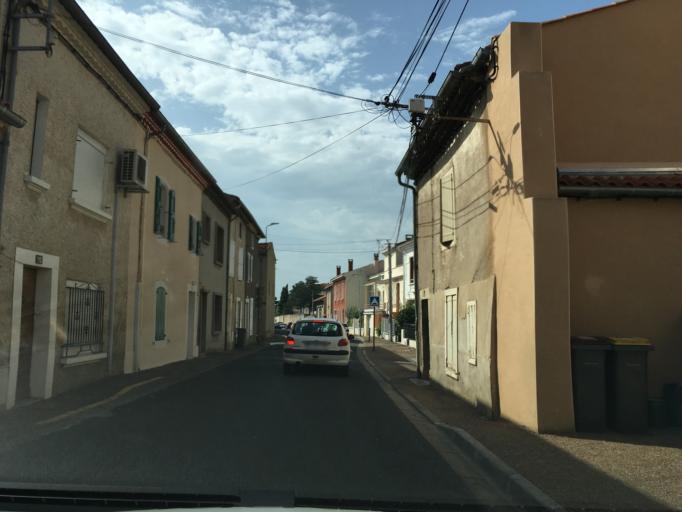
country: FR
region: Midi-Pyrenees
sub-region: Departement du Tarn
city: Castres
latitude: 43.6039
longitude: 2.2520
